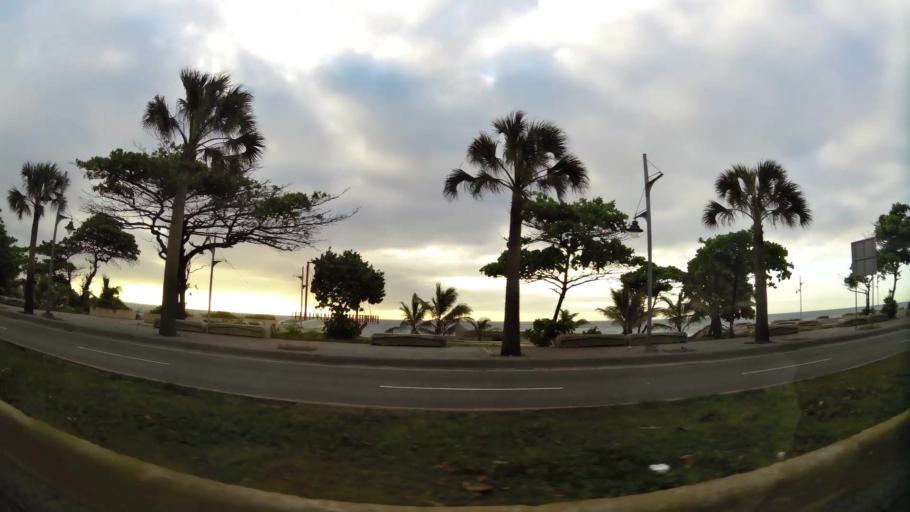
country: DO
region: Nacional
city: La Julia
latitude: 18.4482
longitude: -69.9235
